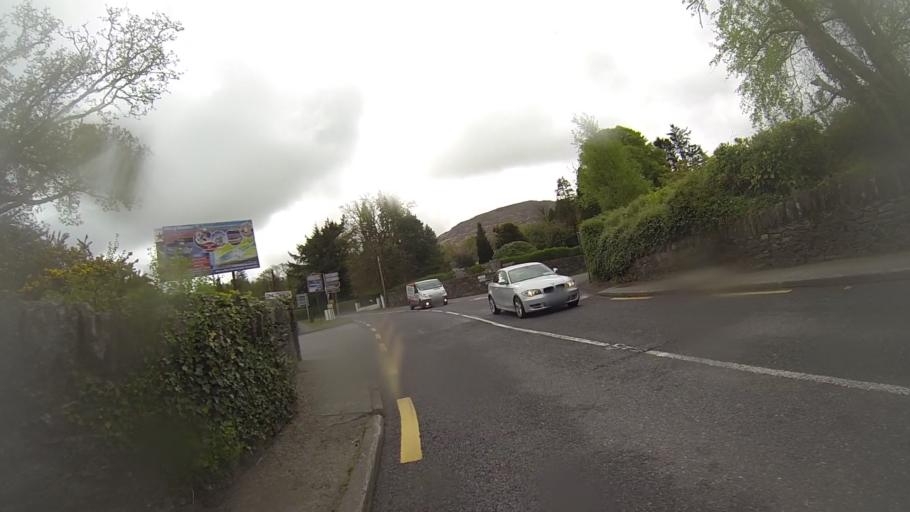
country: IE
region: Munster
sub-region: Ciarrai
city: Kenmare
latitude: 51.8707
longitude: -9.5815
